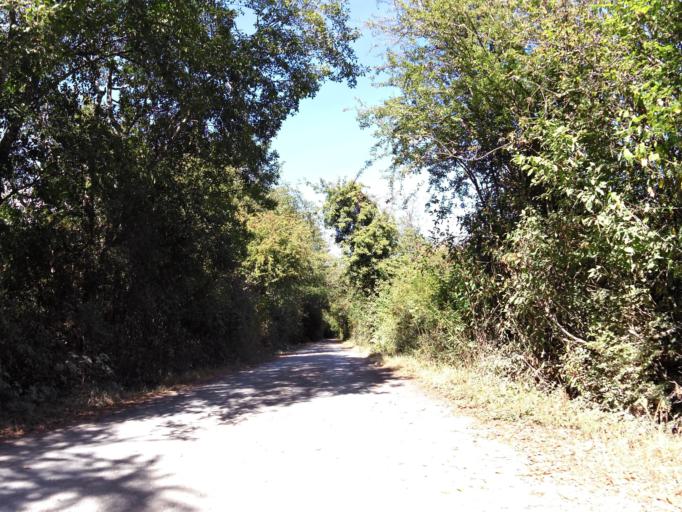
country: CA
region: British Columbia
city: Victoria
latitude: 48.5437
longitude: -123.3837
